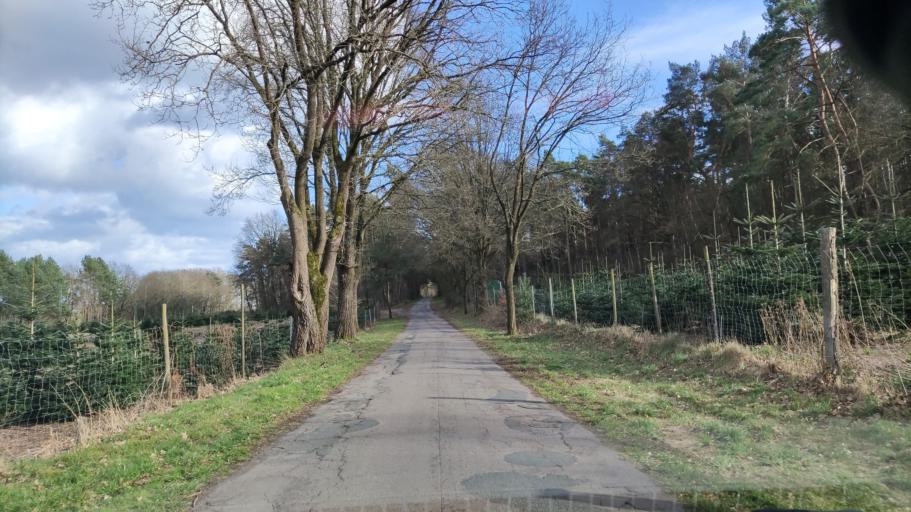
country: DE
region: Lower Saxony
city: Jelmstorf
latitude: 53.1268
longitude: 10.5141
